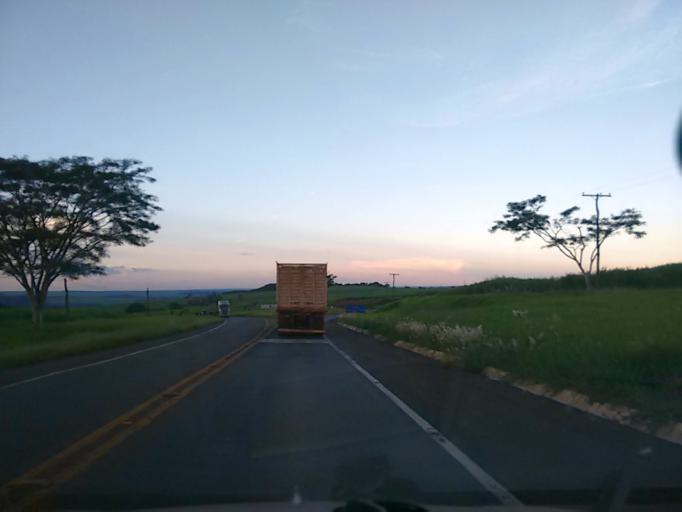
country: BR
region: Sao Paulo
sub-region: Boa Esperanca Do Sul
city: Boa Esperanca do Sul
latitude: -22.1223
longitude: -48.4570
